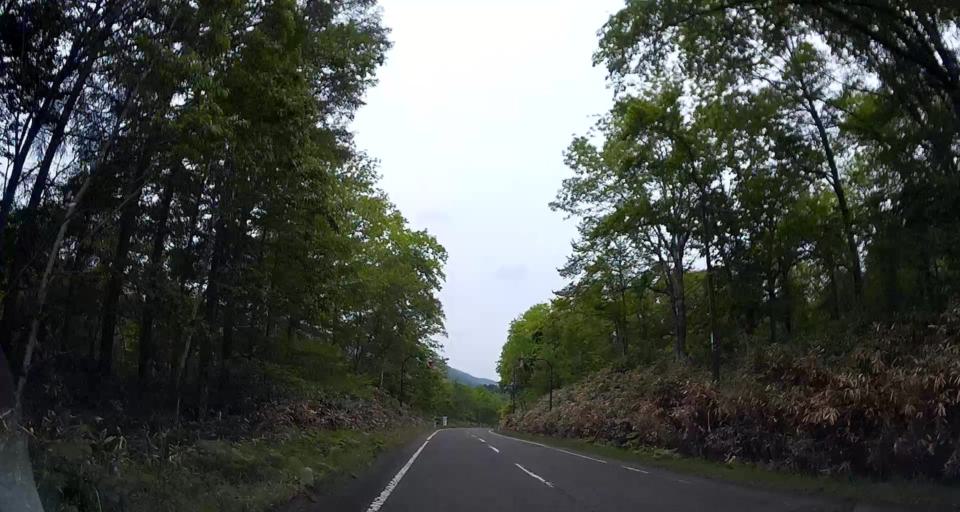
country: JP
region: Hokkaido
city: Shiraoi
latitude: 42.6396
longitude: 141.2285
